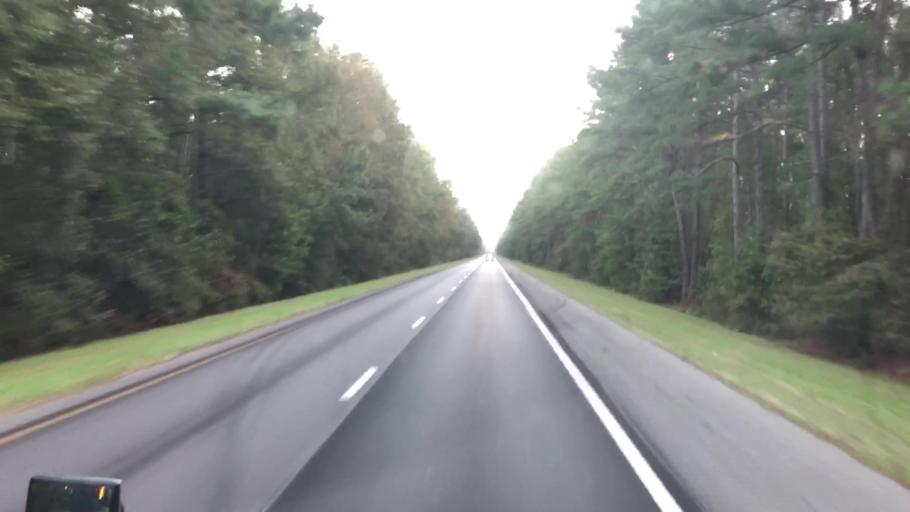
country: US
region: South Carolina
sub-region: Orangeburg County
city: Holly Hill
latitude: 33.5550
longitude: -80.4024
